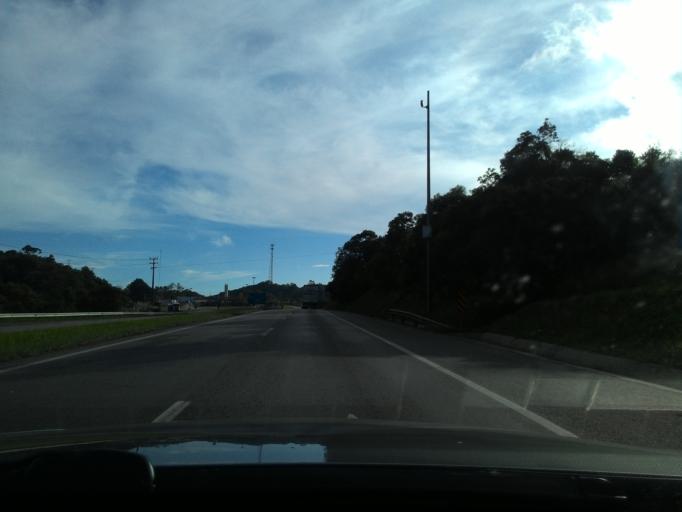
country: BR
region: Parana
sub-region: Campina Grande Do Sul
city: Campina Grande do Sul
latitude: -25.2959
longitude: -48.9377
